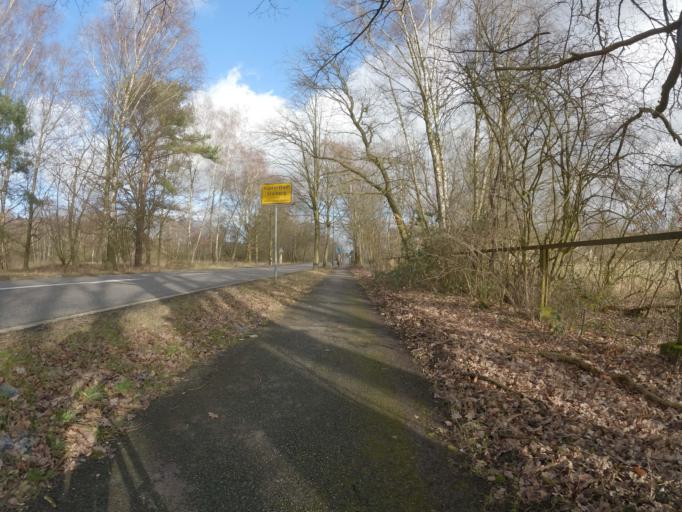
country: DE
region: North Rhine-Westphalia
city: Stolberg
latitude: 50.7791
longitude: 6.1952
